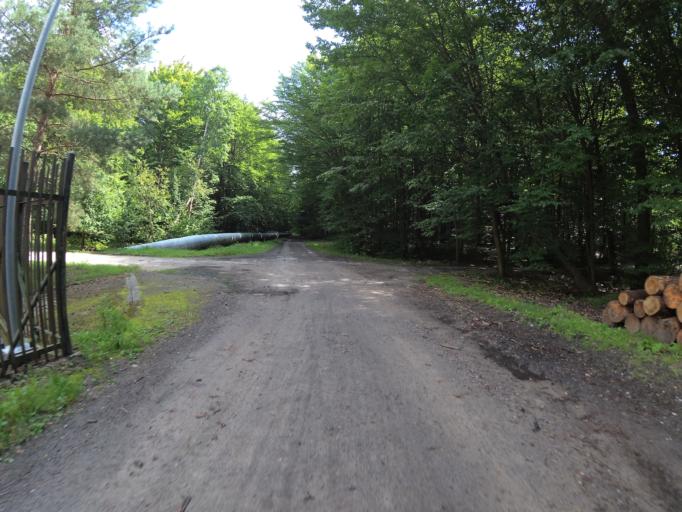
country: PL
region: Pomeranian Voivodeship
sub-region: Gdynia
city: Wielki Kack
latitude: 54.5125
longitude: 18.4799
